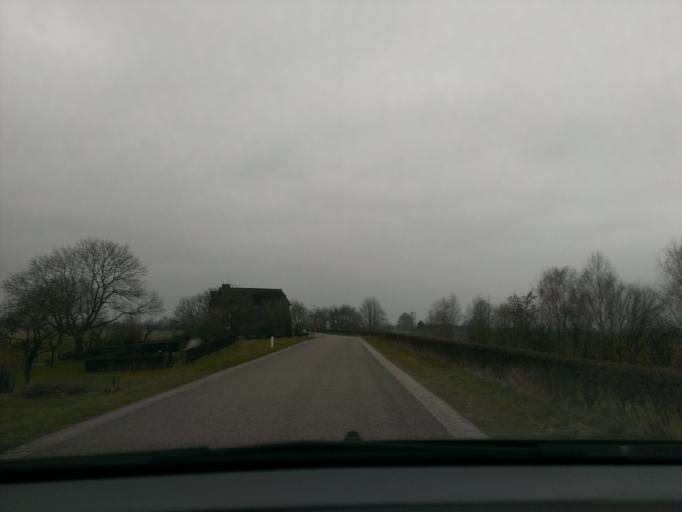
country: NL
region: Overijssel
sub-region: Gemeente Olst-Wijhe
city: Wijhe
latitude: 52.3943
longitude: 6.1234
